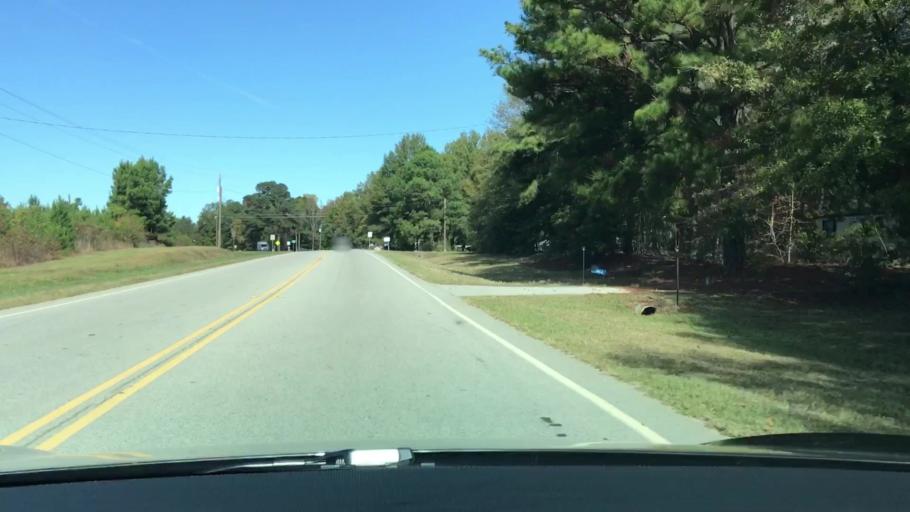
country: US
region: Georgia
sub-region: Warren County
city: Firing Range
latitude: 33.4553
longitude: -82.6981
